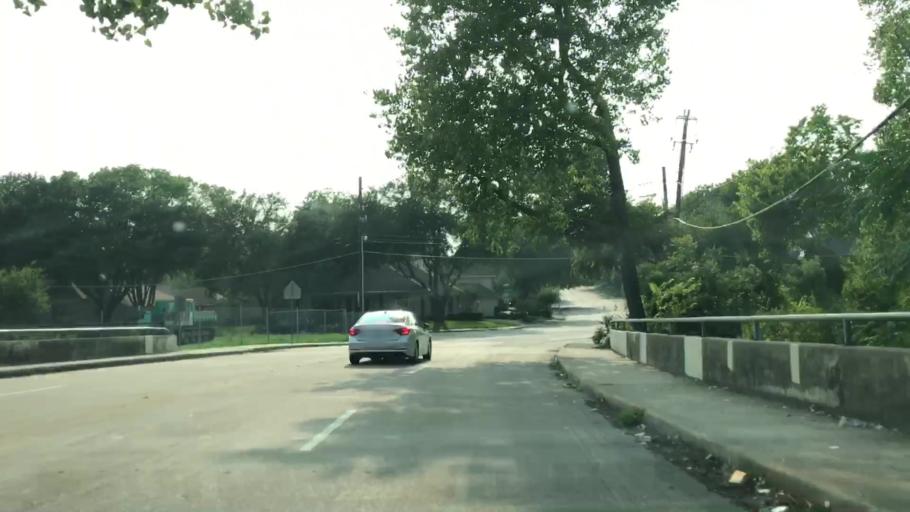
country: US
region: Texas
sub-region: Dallas County
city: Richardson
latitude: 32.9012
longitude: -96.7275
